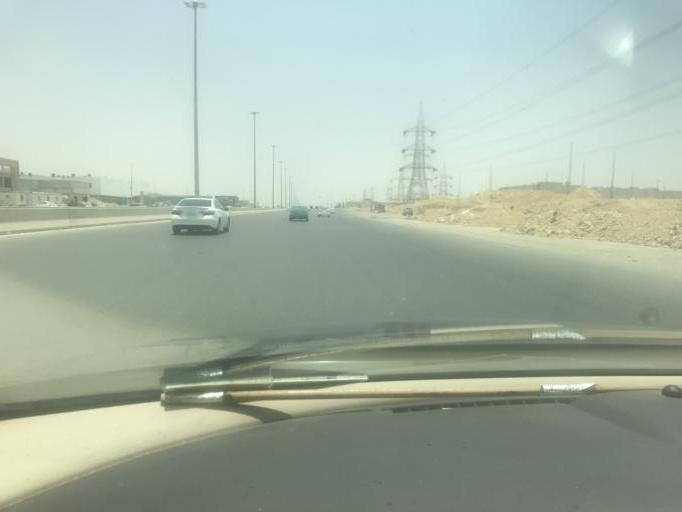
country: SA
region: Ar Riyad
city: Riyadh
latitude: 24.8148
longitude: 46.7281
